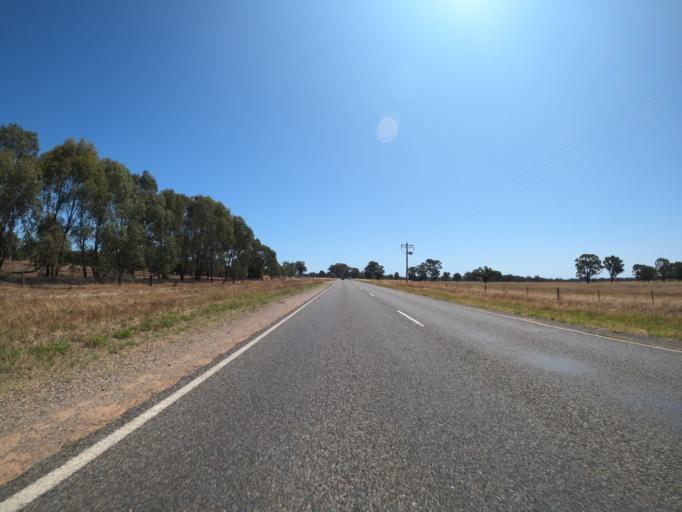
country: AU
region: New South Wales
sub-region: Corowa Shire
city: Corowa
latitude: -36.0662
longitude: 146.3662
